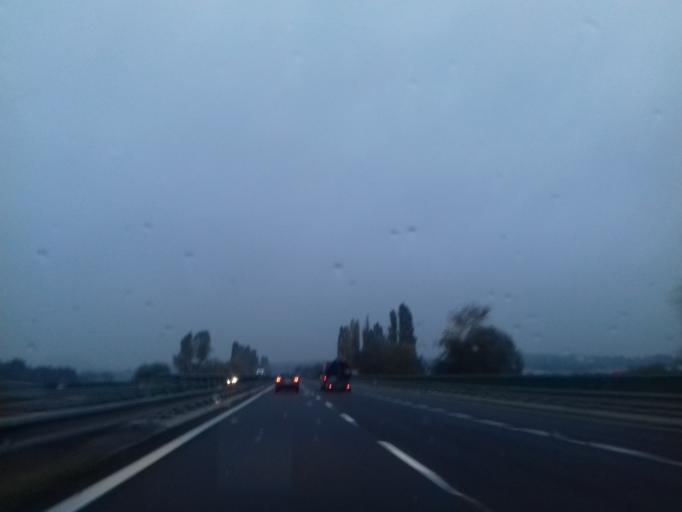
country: CZ
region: Olomoucky
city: Litovel
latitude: 49.6905
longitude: 17.0496
